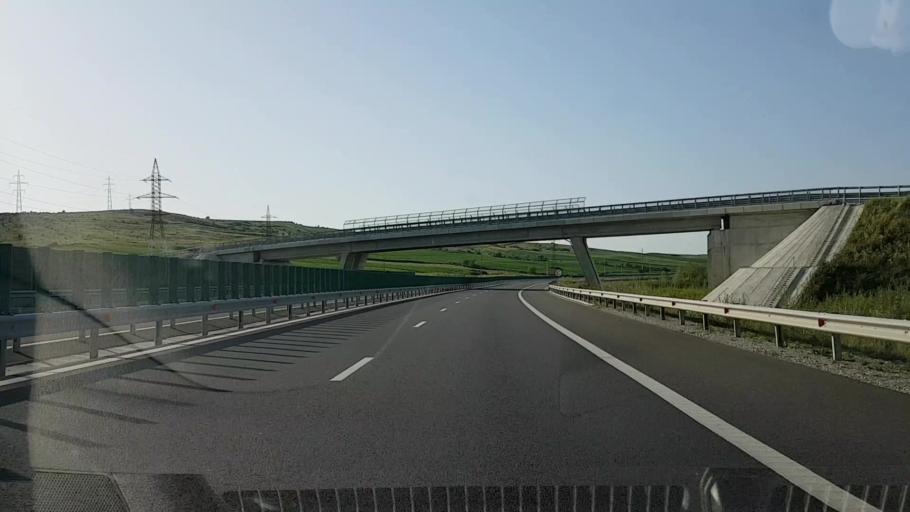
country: RO
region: Cluj
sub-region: Comuna Mihai Viteazu
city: Mihai Viteazu
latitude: 46.4677
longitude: 23.7779
